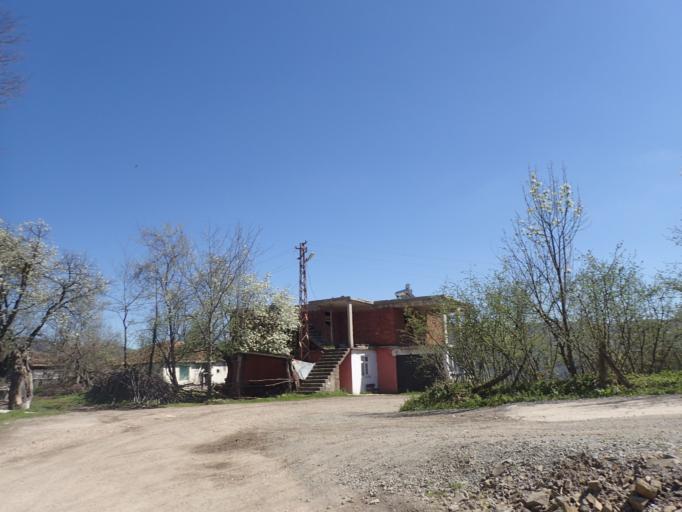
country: TR
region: Ordu
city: Korgan
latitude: 40.7592
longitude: 37.3080
